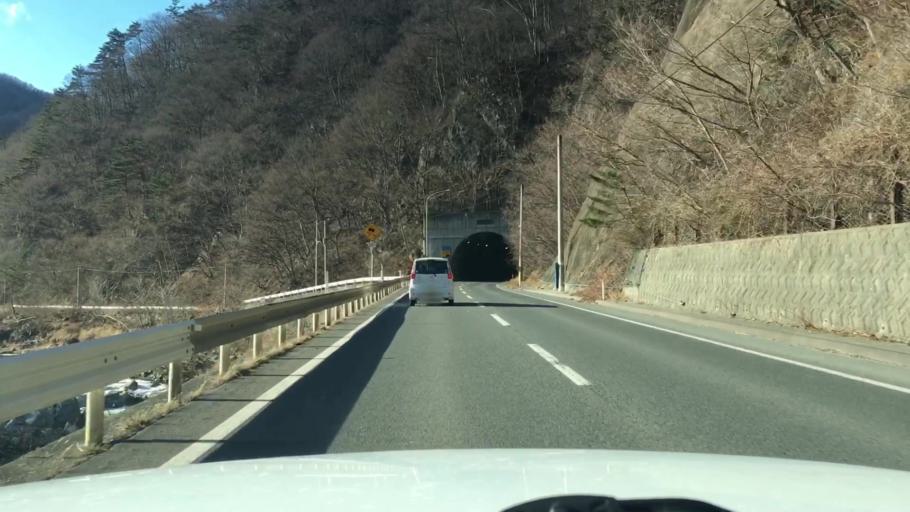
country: JP
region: Iwate
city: Miyako
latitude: 39.5969
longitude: 141.7163
